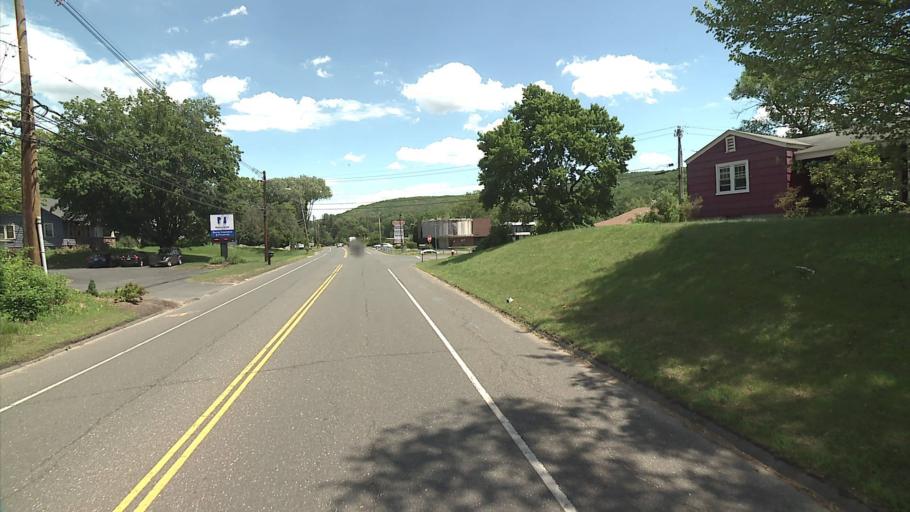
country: US
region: Connecticut
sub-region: New Haven County
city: Naugatuck
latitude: 41.4679
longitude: -73.0216
